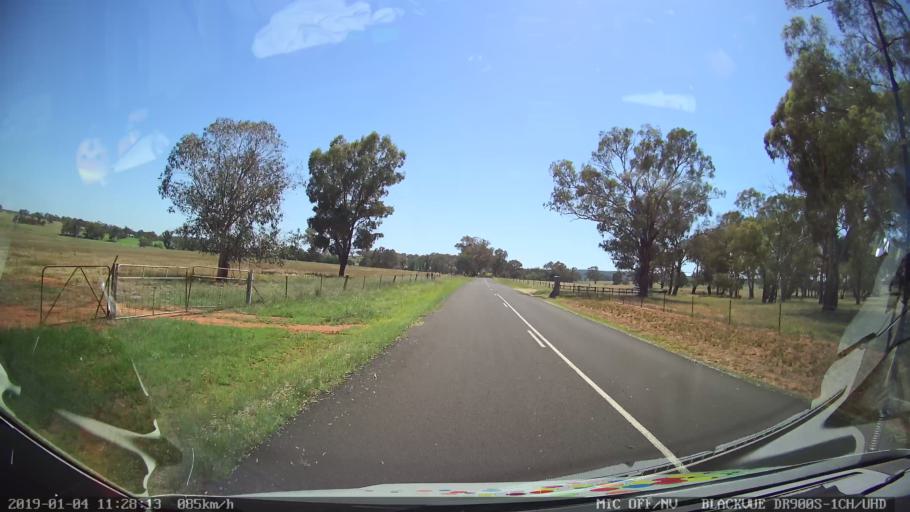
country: AU
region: New South Wales
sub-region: Cabonne
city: Molong
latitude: -33.1017
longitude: 148.7700
